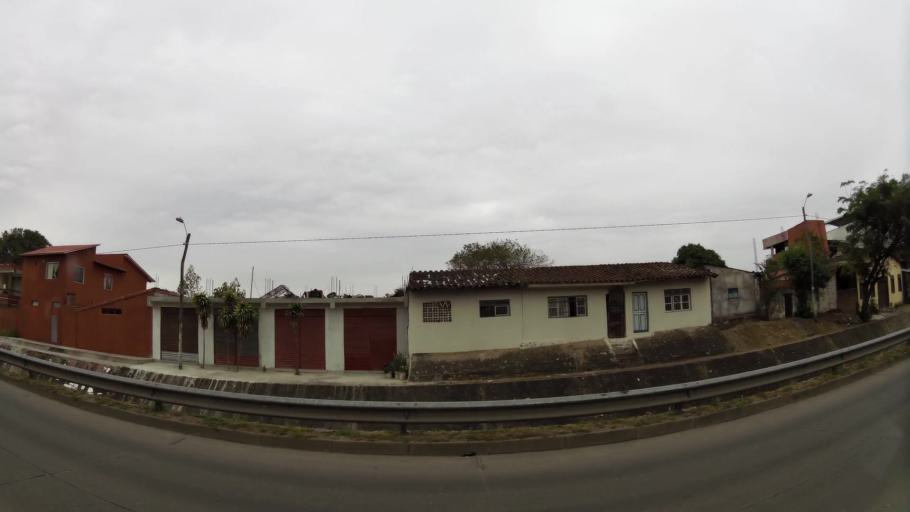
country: BO
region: Santa Cruz
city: Santa Cruz de la Sierra
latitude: -17.7768
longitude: -63.2052
